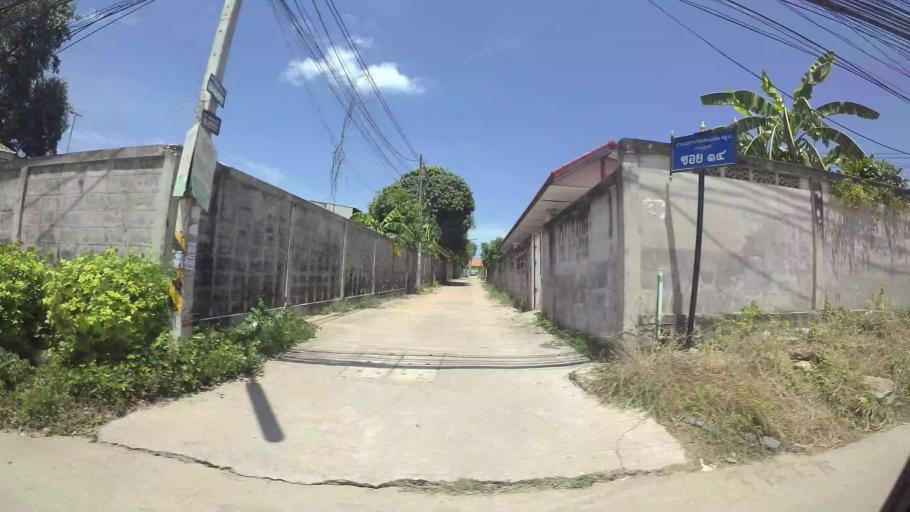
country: TH
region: Chon Buri
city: Ban Talat Bueng
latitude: 13.1152
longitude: 100.9587
